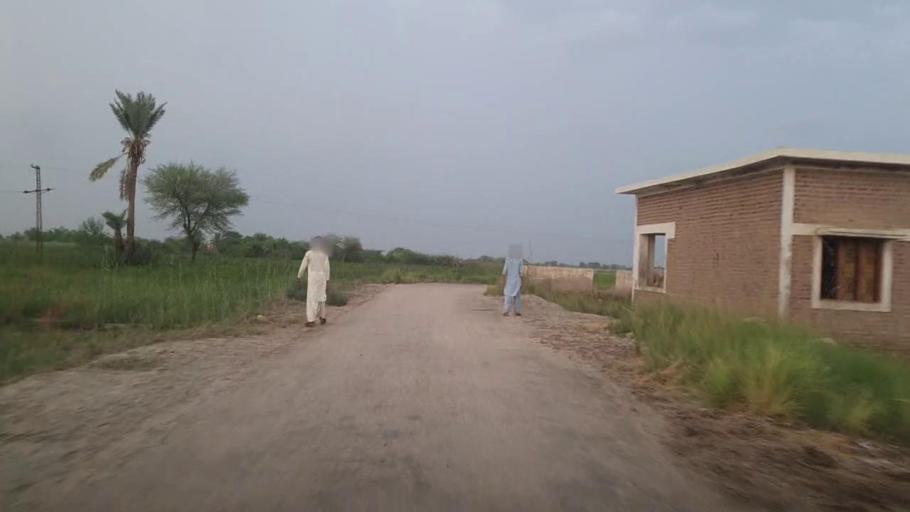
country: PK
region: Sindh
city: Karaundi
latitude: 27.0035
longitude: 68.3450
